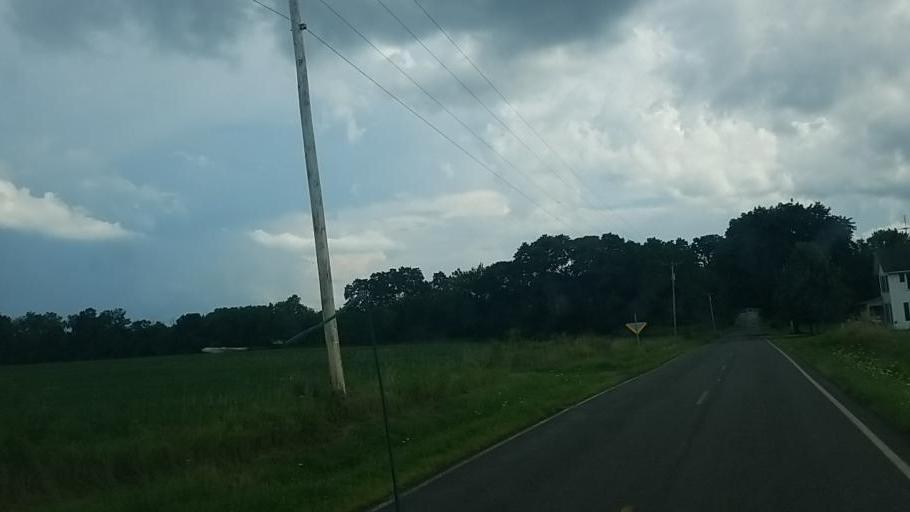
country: US
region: Ohio
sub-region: Medina County
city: Westfield Center
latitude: 41.0083
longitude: -81.9410
